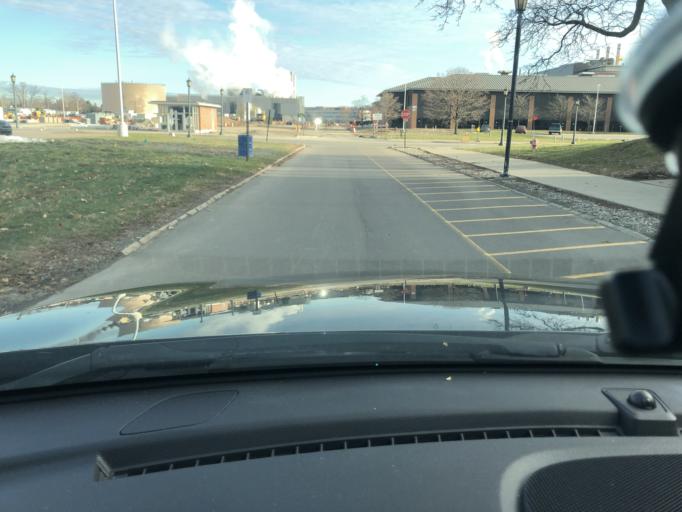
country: US
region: Michigan
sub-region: Wayne County
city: Allen Park
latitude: 42.2981
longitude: -83.2365
